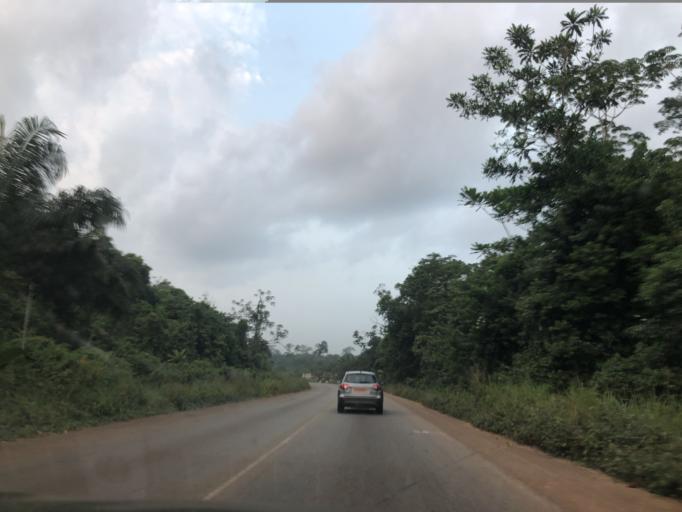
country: CM
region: Littoral
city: Edea
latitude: 3.9139
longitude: 10.0607
